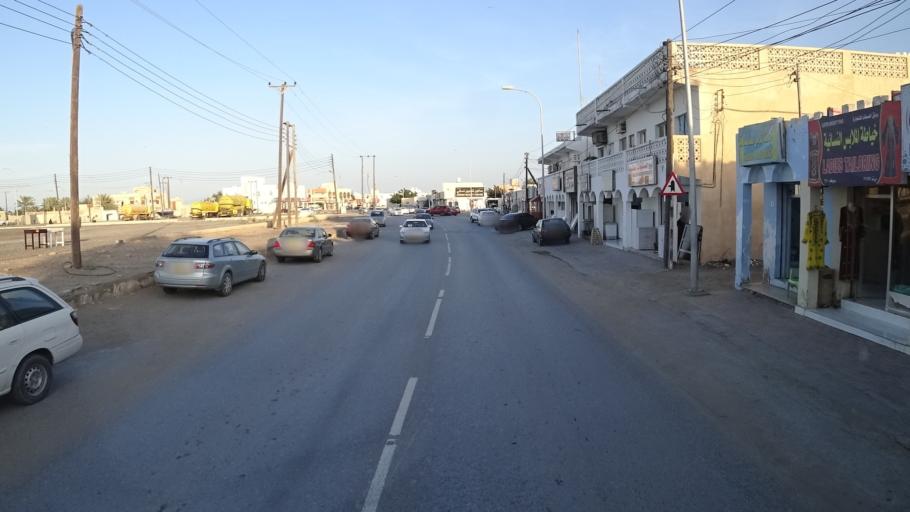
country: OM
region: Al Batinah
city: Barka'
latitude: 23.7071
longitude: 57.8952
